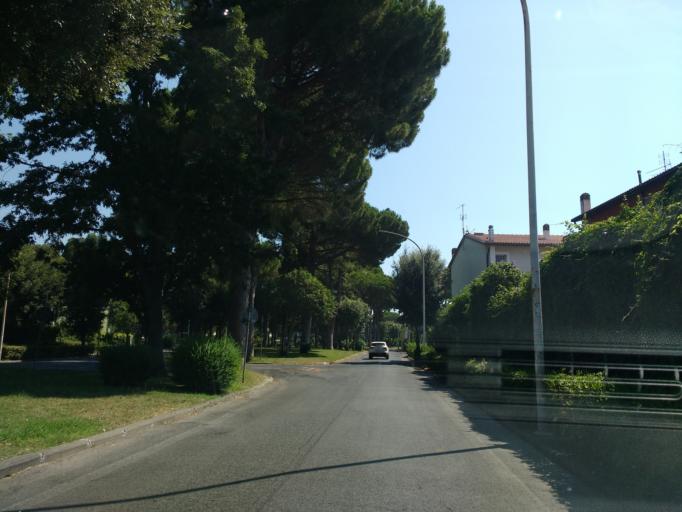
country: IT
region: Latium
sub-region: Citta metropolitana di Roma Capitale
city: Acilia-Castel Fusano-Ostia Antica
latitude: 41.7577
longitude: 12.3575
